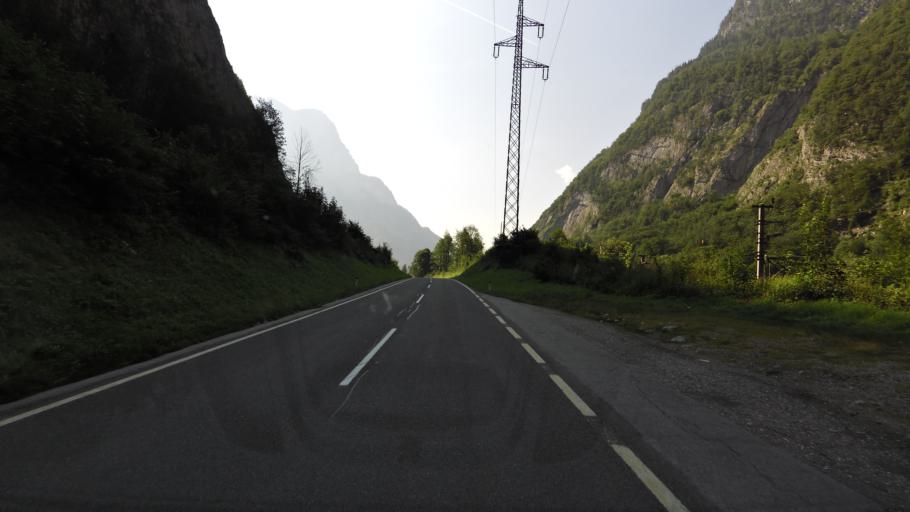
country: AT
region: Salzburg
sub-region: Politischer Bezirk Hallein
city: Golling an der Salzach
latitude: 47.5582
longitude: 13.1662
